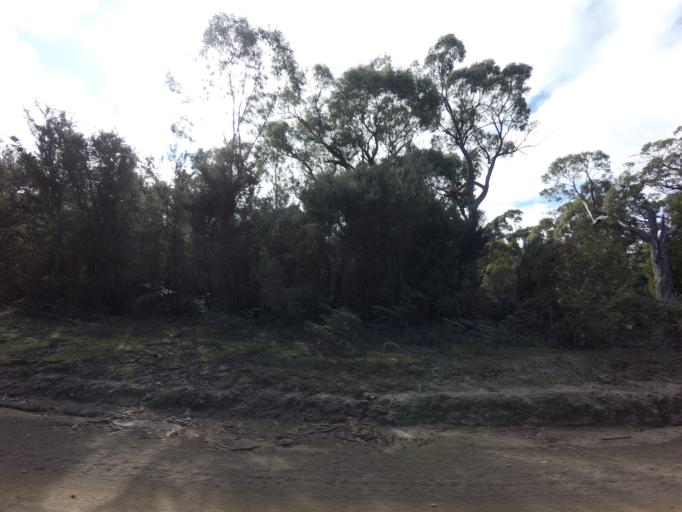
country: AU
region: Tasmania
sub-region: Clarence
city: Sandford
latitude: -43.0879
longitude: 147.6982
